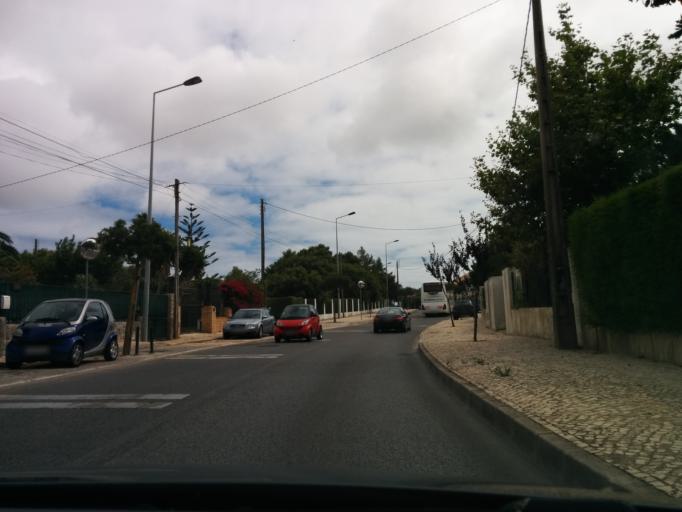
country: PT
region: Lisbon
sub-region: Cascais
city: Alcabideche
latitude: 38.7276
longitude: -9.4437
